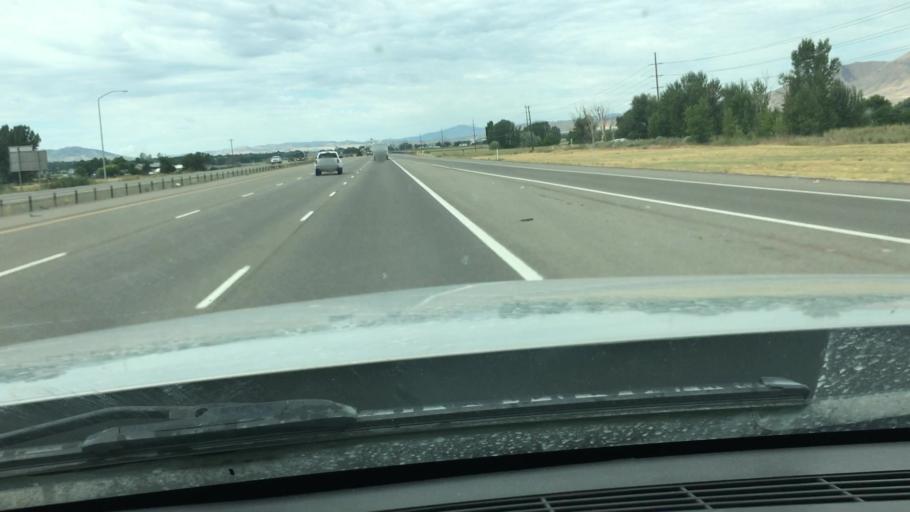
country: US
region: Utah
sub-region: Utah County
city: Benjamin
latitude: 40.0816
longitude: -111.7067
